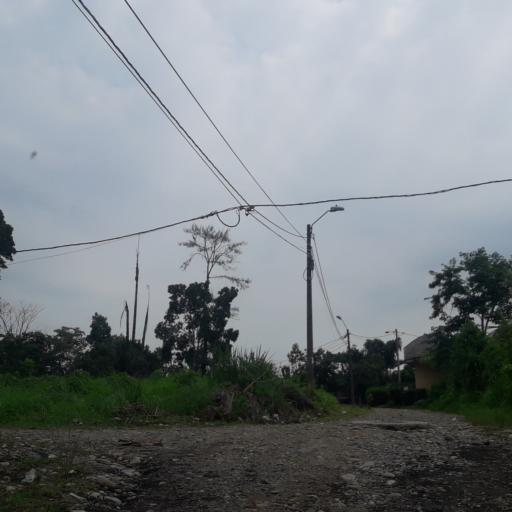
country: EC
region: Napo
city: Tena
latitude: -0.9821
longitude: -77.8159
